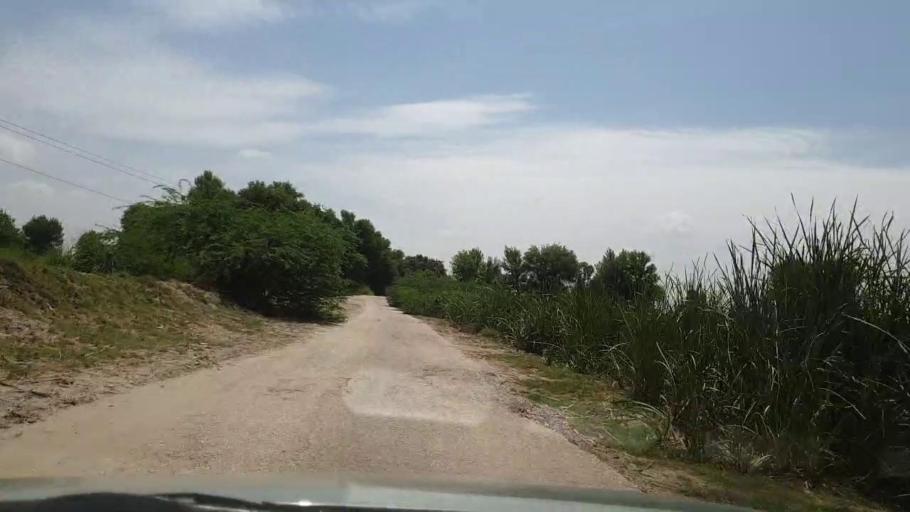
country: PK
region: Sindh
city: Bozdar
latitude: 27.0765
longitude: 68.9695
